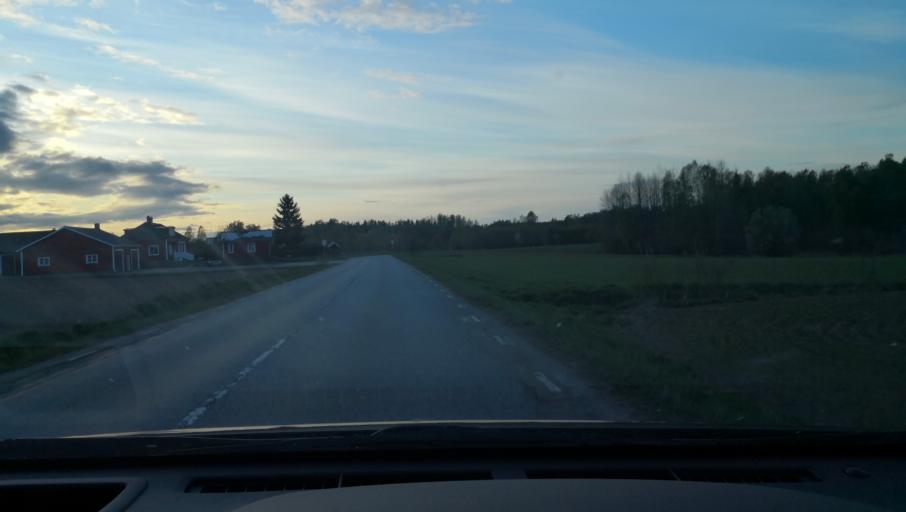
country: SE
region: OErebro
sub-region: Askersunds Kommun
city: Asbro
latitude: 58.9287
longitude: 15.0310
